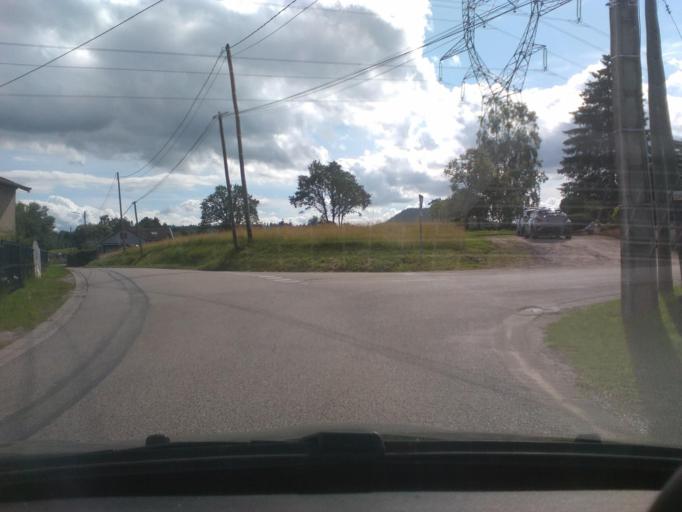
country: FR
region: Lorraine
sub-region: Departement des Vosges
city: Bruyeres
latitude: 48.2211
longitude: 6.7590
